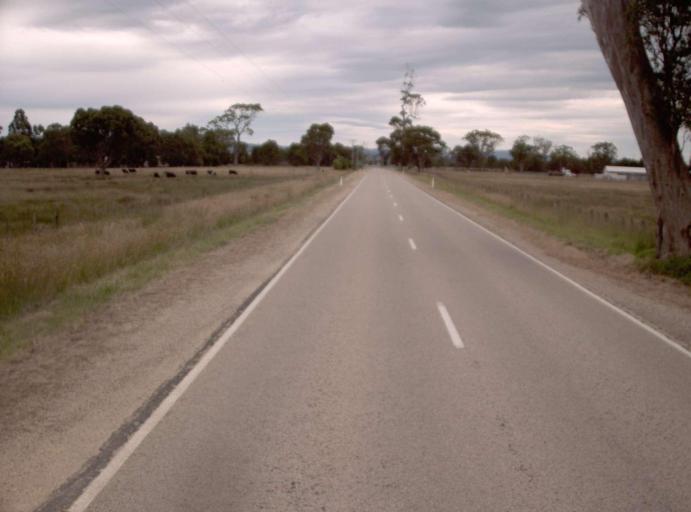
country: AU
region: Victoria
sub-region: East Gippsland
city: Bairnsdale
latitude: -37.8523
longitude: 147.5653
